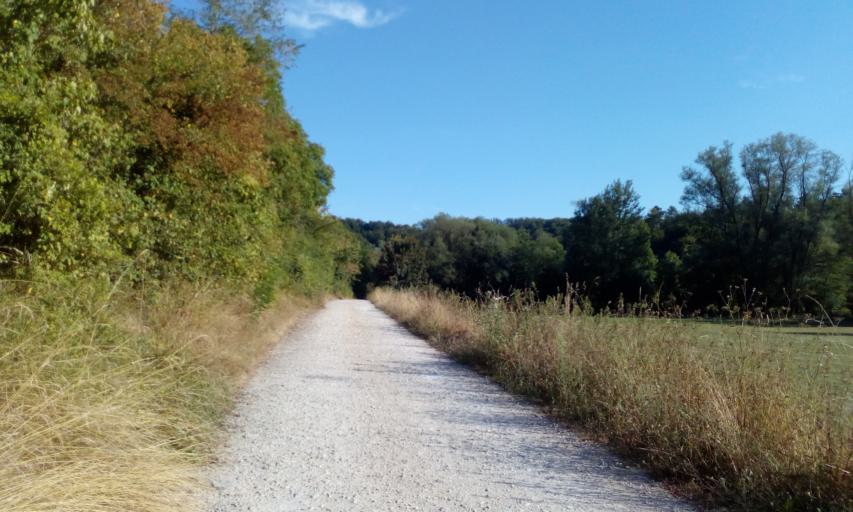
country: FR
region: Lorraine
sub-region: Departement de Meurthe-et-Moselle
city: Pagny-sur-Moselle
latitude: 48.9681
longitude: 5.8865
